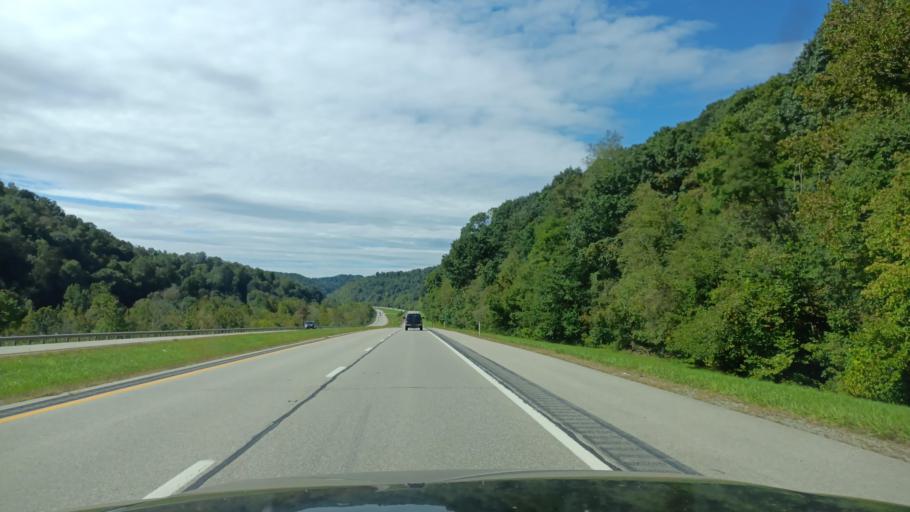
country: US
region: West Virginia
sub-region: Doddridge County
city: West Union
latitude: 39.2854
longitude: -80.7021
